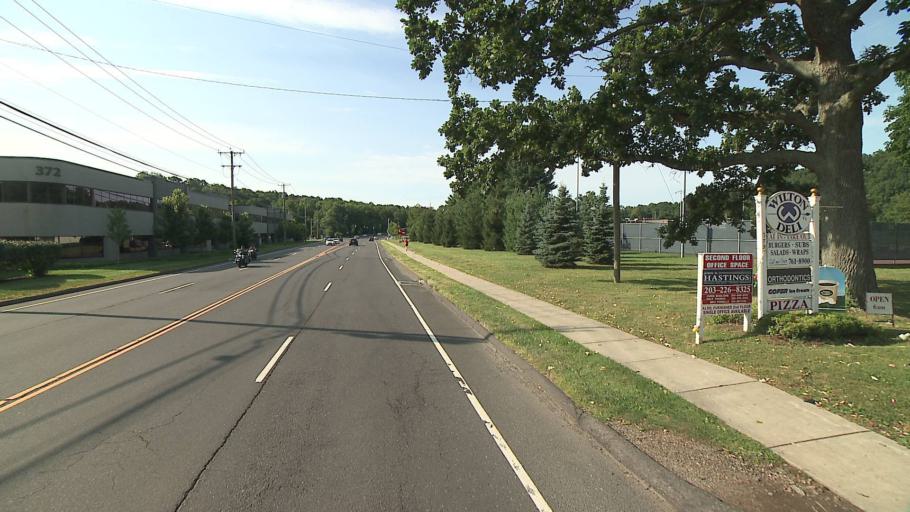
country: US
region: Connecticut
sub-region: Fairfield County
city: Wilton
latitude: 41.2080
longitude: -73.4311
